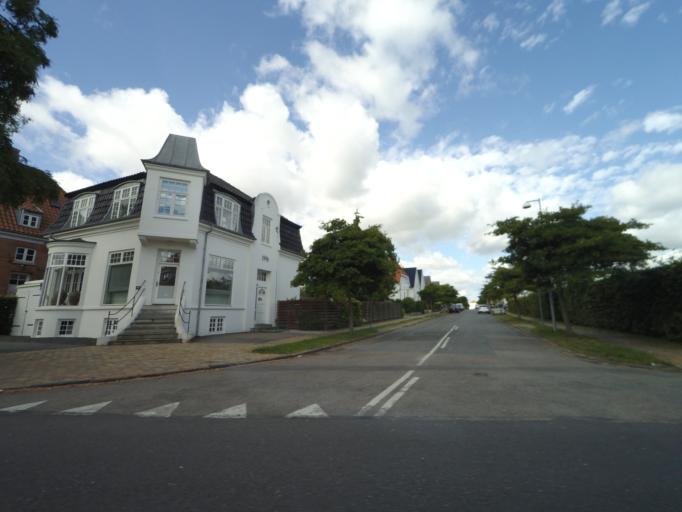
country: DK
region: South Denmark
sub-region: Odense Kommune
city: Odense
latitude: 55.3840
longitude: 10.3894
